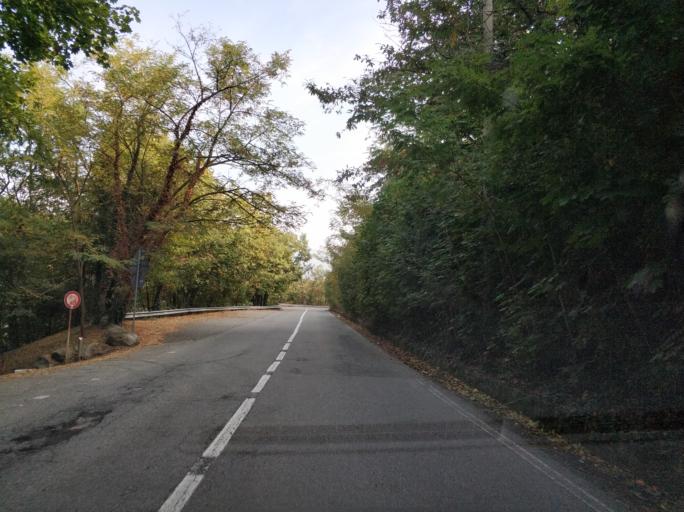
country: IT
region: Piedmont
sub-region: Provincia di Torino
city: Ivrea
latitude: 45.4822
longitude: 7.8812
